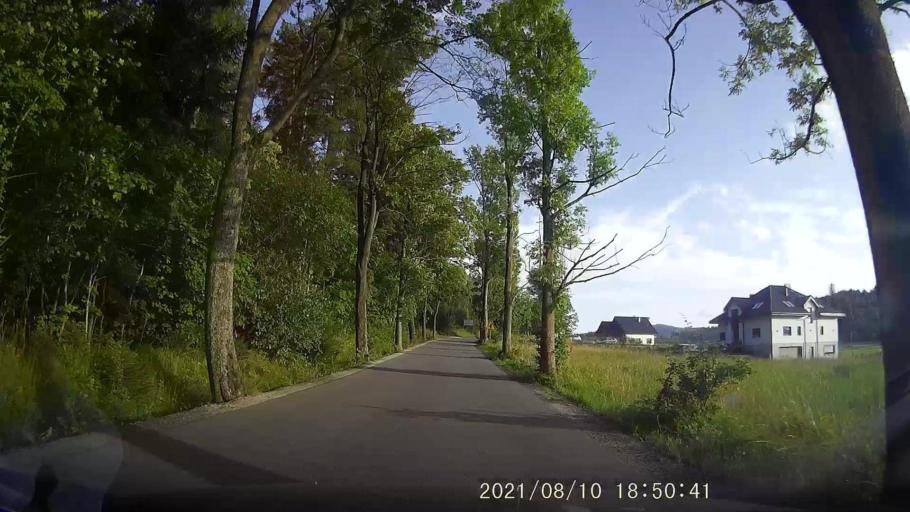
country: PL
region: Lower Silesian Voivodeship
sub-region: Powiat klodzki
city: Duszniki-Zdroj
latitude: 50.4171
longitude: 16.3778
